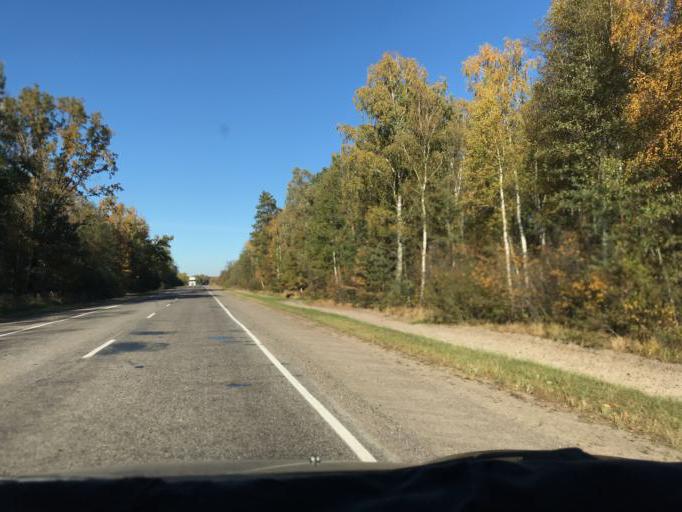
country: BY
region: Gomel
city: Yel'sk
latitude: 51.7282
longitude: 29.1725
